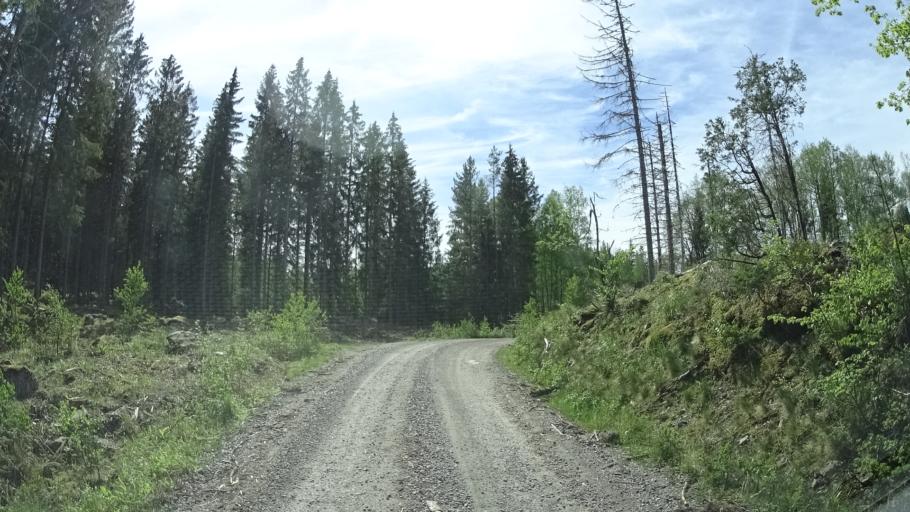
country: SE
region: OEstergoetland
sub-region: Finspangs Kommun
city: Finspang
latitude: 58.7866
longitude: 15.8470
